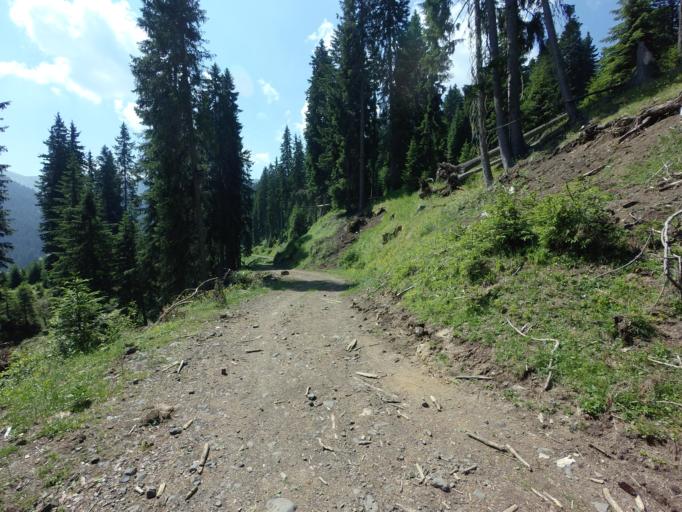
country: IT
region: Trentino-Alto Adige
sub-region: Bolzano
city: Ortisei
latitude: 46.5225
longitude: 11.6587
